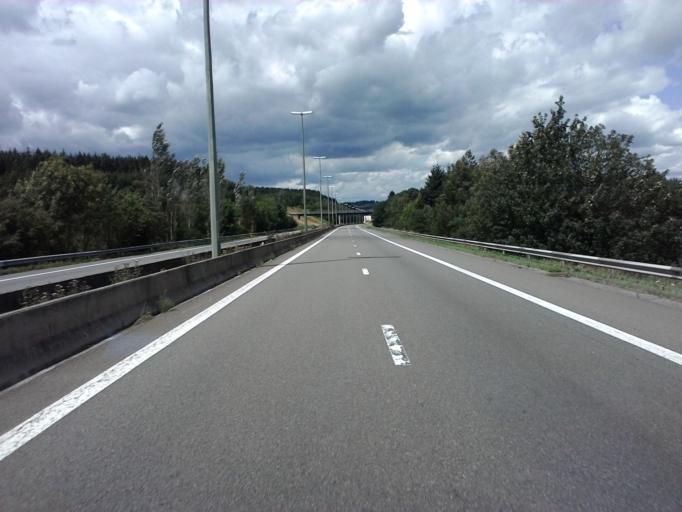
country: BE
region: Wallonia
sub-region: Province du Luxembourg
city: Manhay
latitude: 50.3406
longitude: 5.6915
